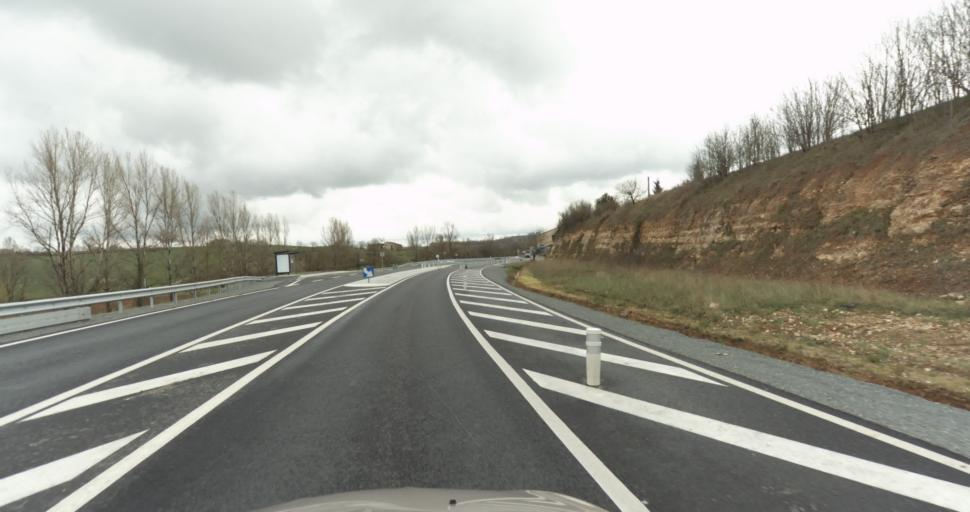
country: FR
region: Midi-Pyrenees
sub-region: Departement du Tarn
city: Frejairolles
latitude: 43.8580
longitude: 2.1898
